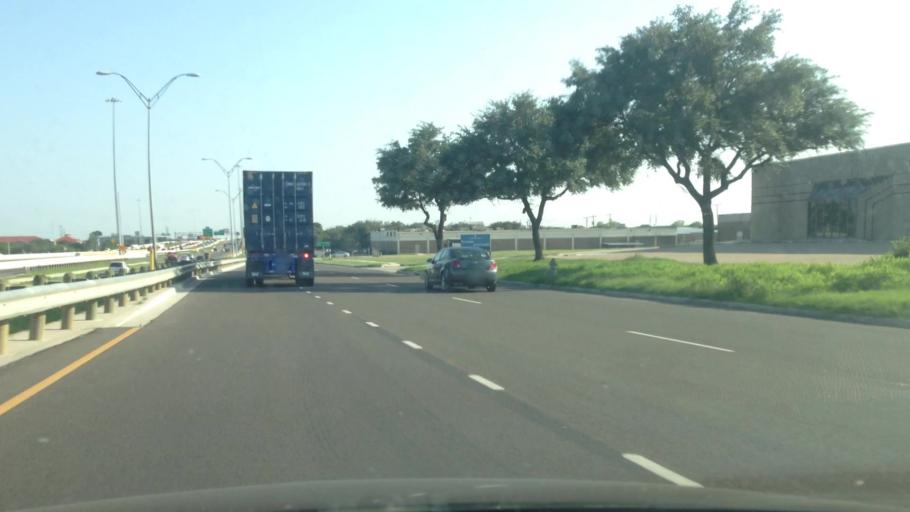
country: US
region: Texas
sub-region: Tarrant County
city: Blue Mound
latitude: 32.8337
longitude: -97.3134
